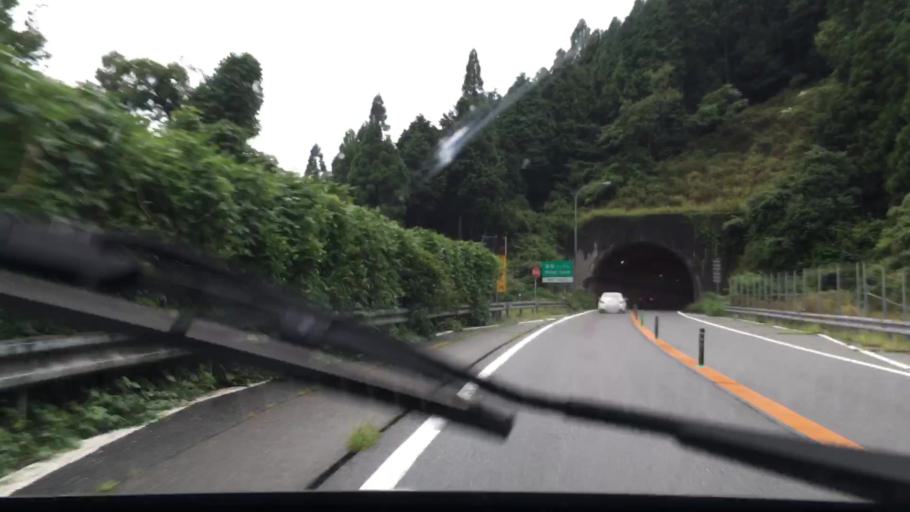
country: JP
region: Hyogo
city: Nishiwaki
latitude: 35.1672
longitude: 134.7892
